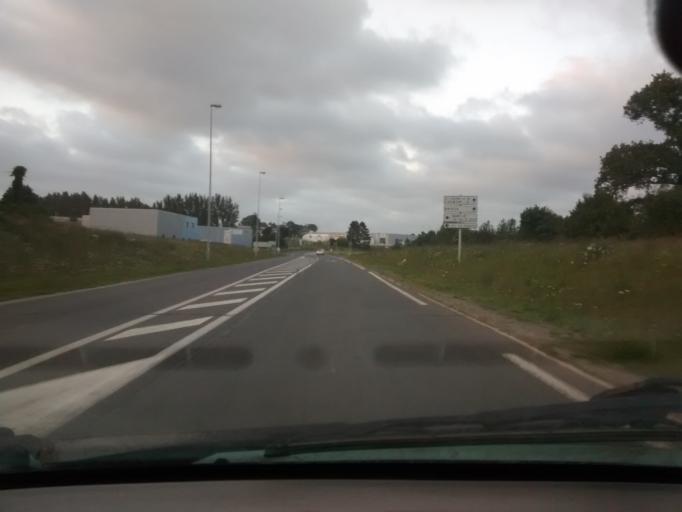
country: FR
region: Lower Normandy
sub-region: Departement de la Manche
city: Saint-Lo
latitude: 49.1089
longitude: -1.0571
